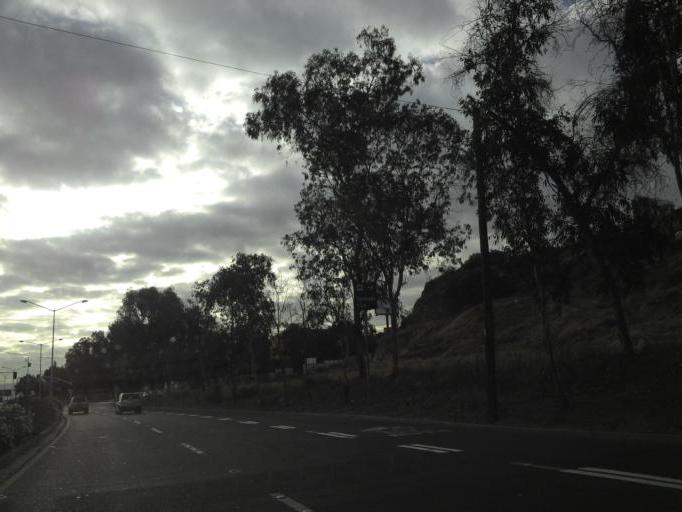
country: MX
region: Baja California
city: Tijuana
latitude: 32.5106
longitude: -116.9935
